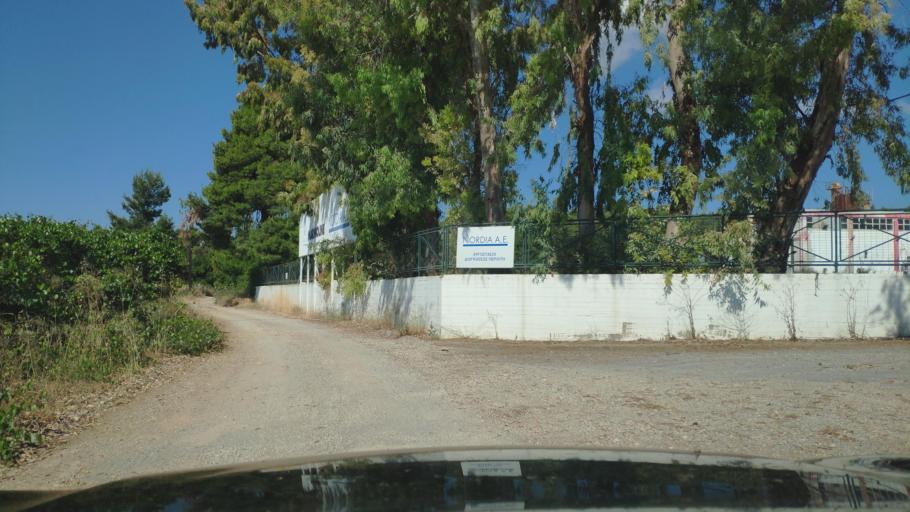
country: GR
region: Central Greece
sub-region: Nomos Voiotias
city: Arma
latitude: 38.3972
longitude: 23.5102
